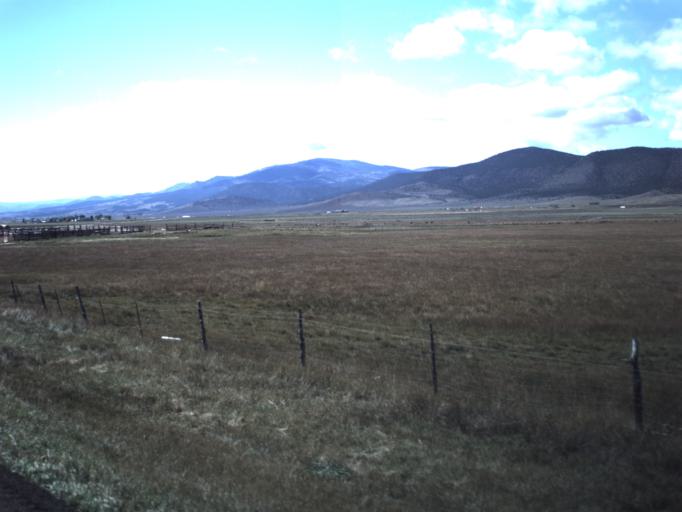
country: US
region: Utah
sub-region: Wayne County
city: Loa
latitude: 38.4945
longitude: -111.8816
